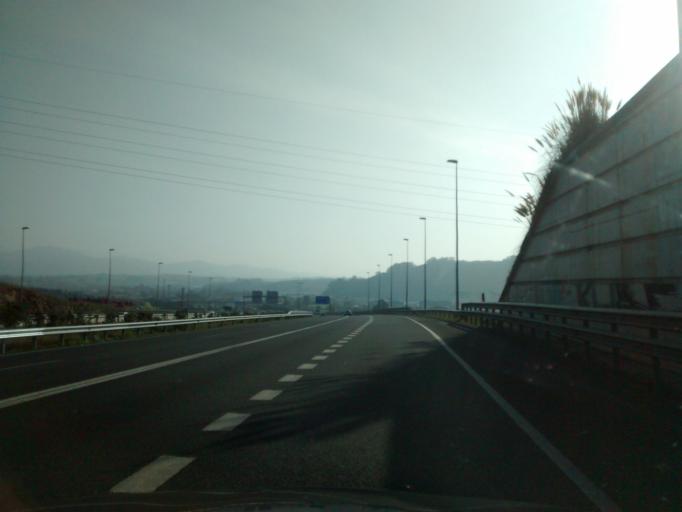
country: ES
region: Cantabria
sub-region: Provincia de Cantabria
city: Santa Cruz de Bezana
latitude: 43.4347
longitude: -3.8764
